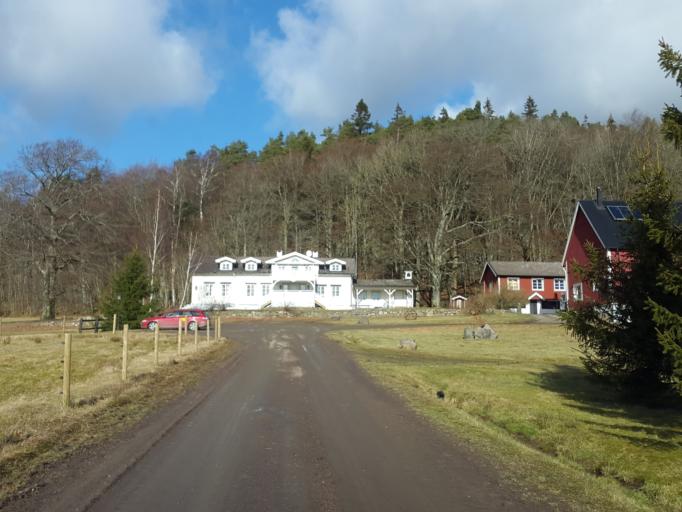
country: SE
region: Vaestra Goetaland
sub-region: Lerums Kommun
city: Olstorp
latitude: 57.8342
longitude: 12.2200
